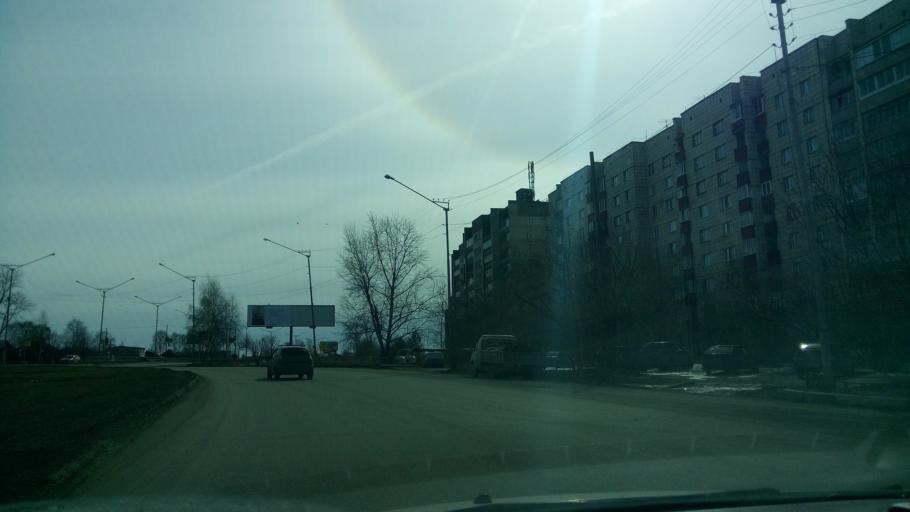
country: RU
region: Sverdlovsk
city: Nizhniy Tagil
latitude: 57.8985
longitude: 59.9372
